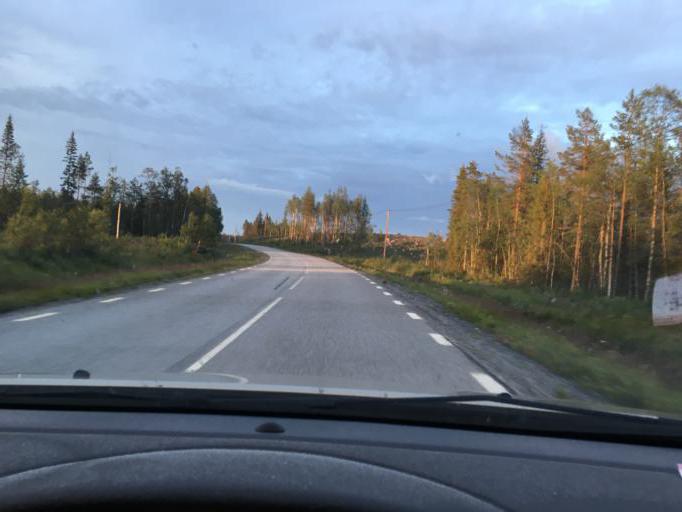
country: SE
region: Norrbotten
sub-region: Lulea Kommun
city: Ranea
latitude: 66.0403
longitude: 22.3089
